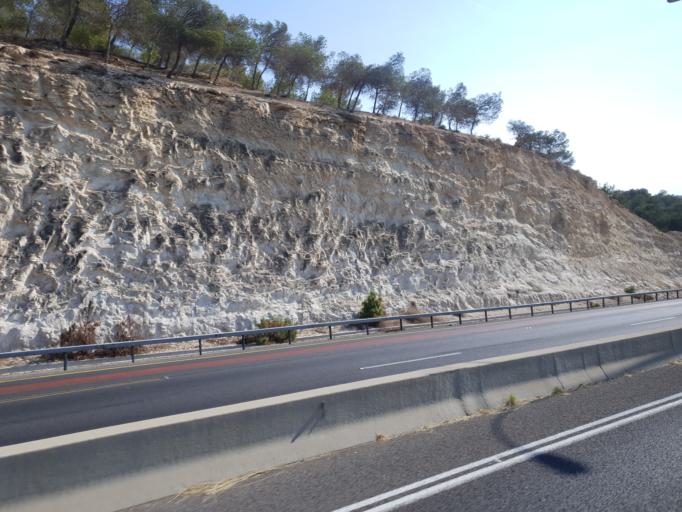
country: PS
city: Az Za`ayyim
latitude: 31.7856
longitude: 35.2807
